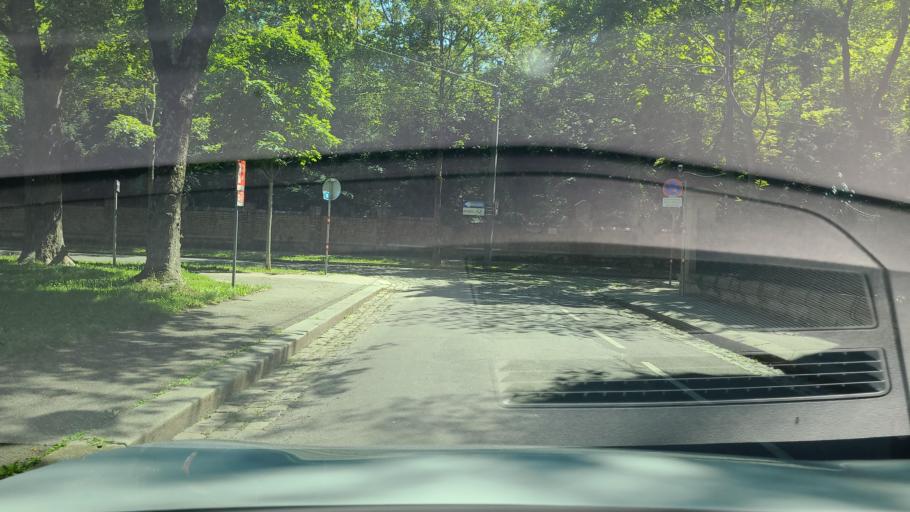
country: AT
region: Vienna
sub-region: Wien Stadt
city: Vienna
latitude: 48.2330
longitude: 16.3338
